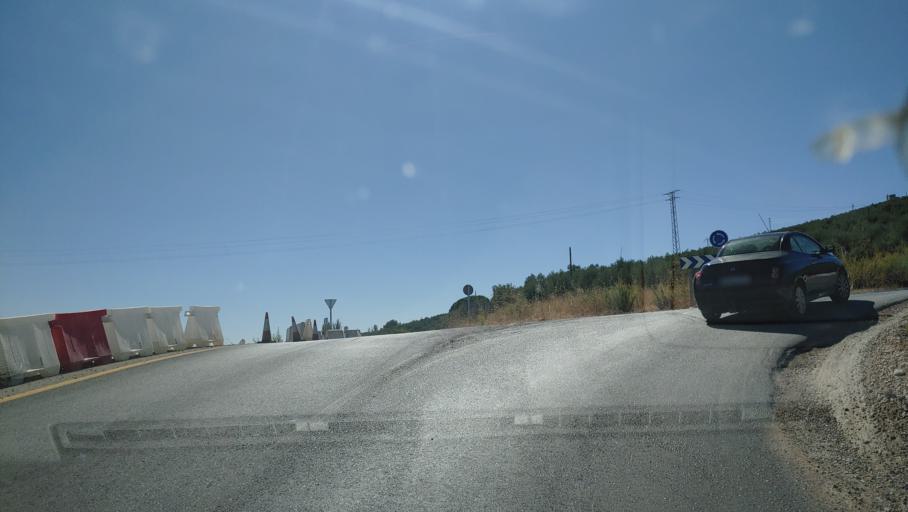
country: ES
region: Andalusia
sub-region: Provincia de Jaen
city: Iznatoraf
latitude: 38.1480
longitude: -3.0231
